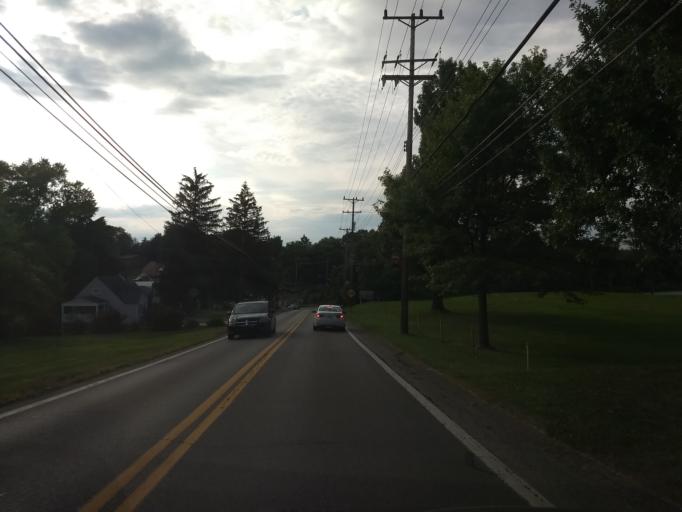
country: US
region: Pennsylvania
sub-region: Allegheny County
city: Coraopolis
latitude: 40.4835
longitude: -80.1363
